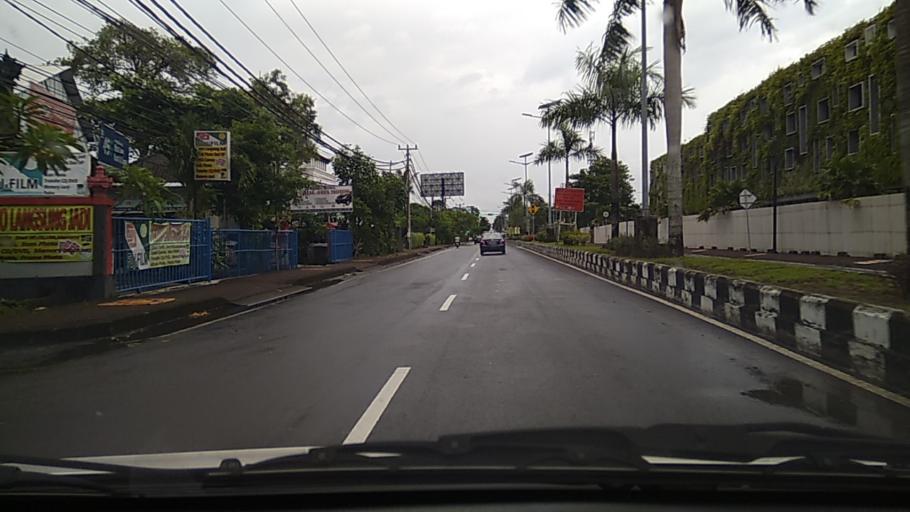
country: ID
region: Bali
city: Bualu
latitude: -8.7945
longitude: 115.2166
